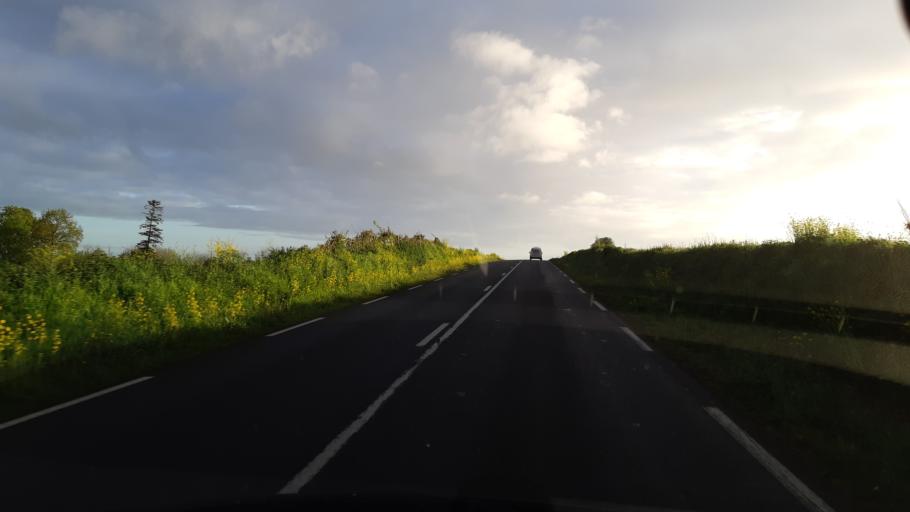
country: FR
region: Lower Normandy
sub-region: Departement de la Manche
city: Agneaux
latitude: 49.0377
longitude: -1.1326
